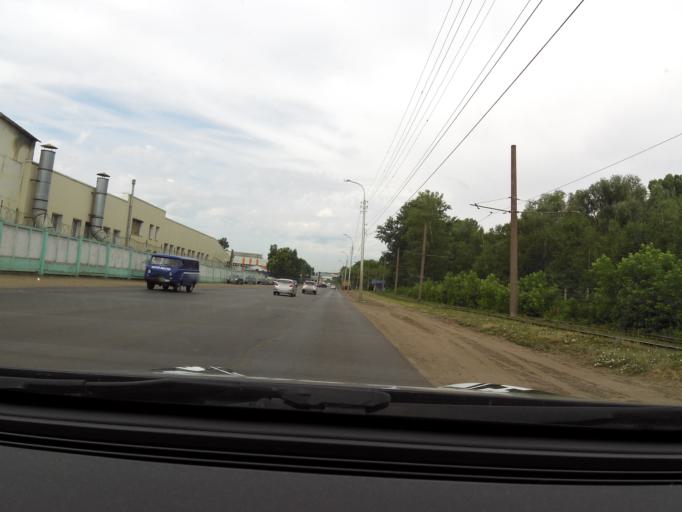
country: RU
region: Bashkortostan
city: Ufa
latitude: 54.7974
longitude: 56.1291
